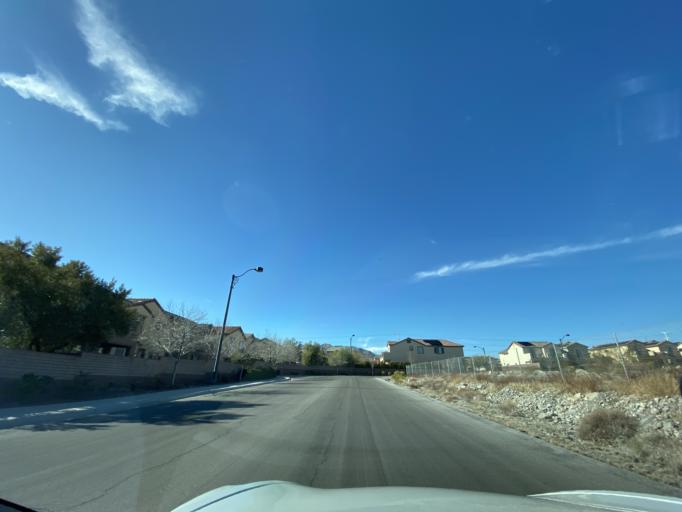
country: US
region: Nevada
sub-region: Clark County
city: Summerlin South
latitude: 36.2956
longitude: -115.3258
